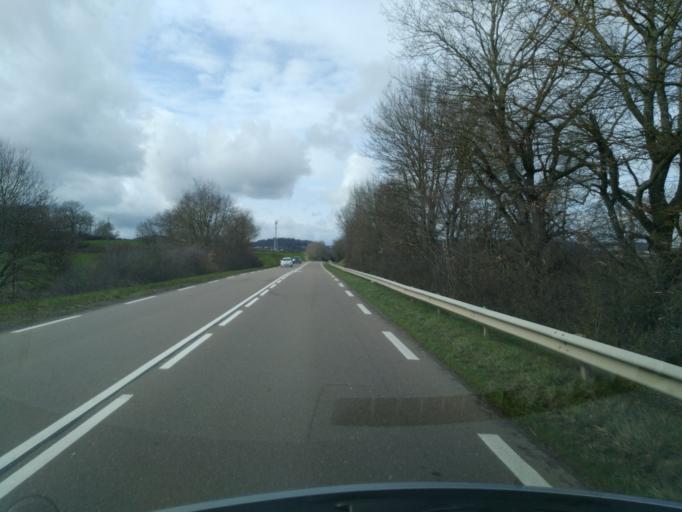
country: FR
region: Bourgogne
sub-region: Departement de Saone-et-Loire
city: Torcy
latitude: 46.7745
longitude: 4.4255
